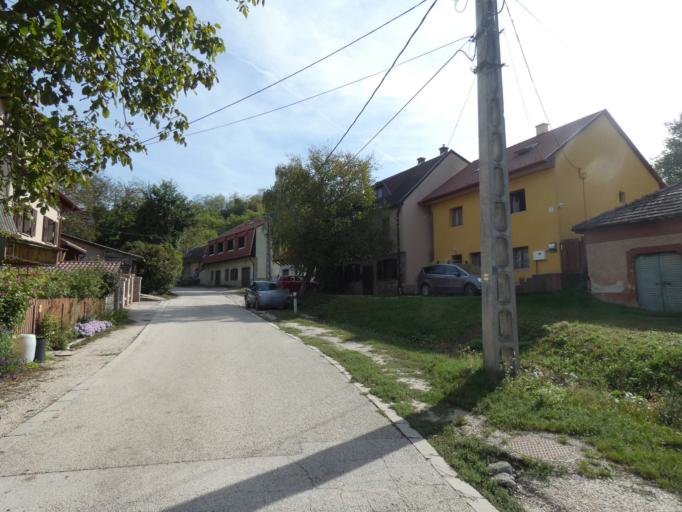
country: HU
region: Komarom-Esztergom
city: Esztergom
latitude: 47.7788
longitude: 18.7594
